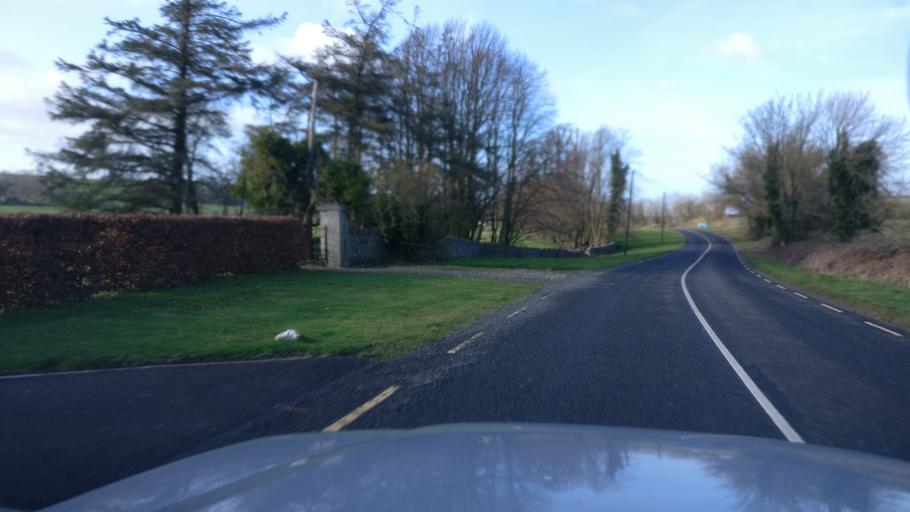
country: IE
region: Leinster
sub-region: Laois
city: Stradbally
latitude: 53.0031
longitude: -7.2261
